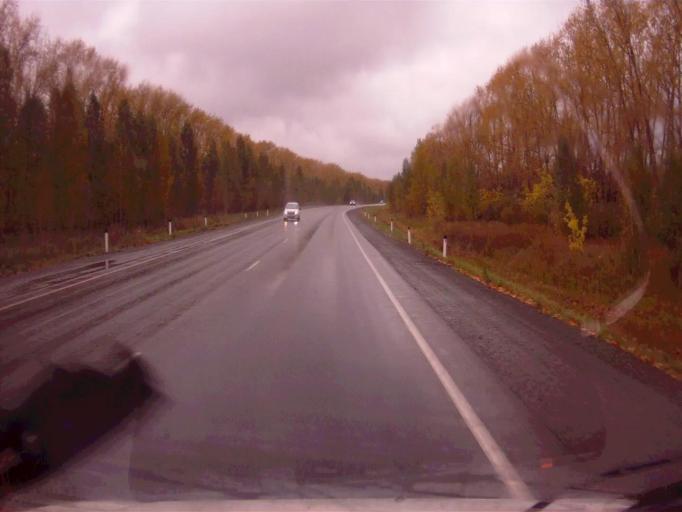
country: RU
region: Chelyabinsk
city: Argayash
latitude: 55.4502
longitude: 60.9387
